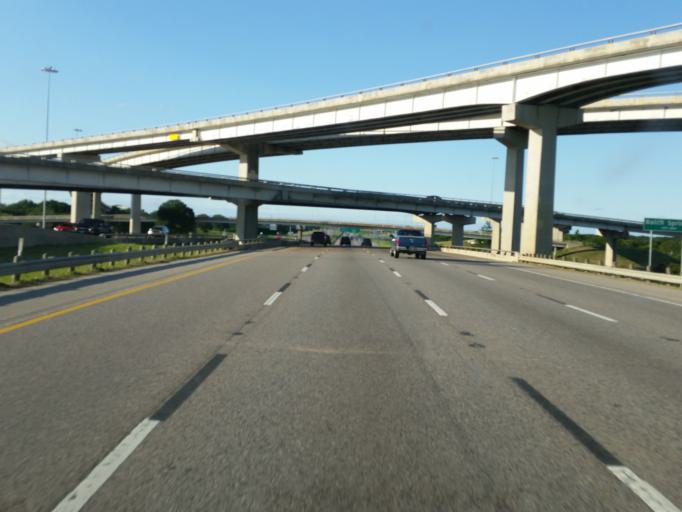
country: US
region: Texas
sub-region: Dallas County
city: Balch Springs
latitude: 32.6906
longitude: -96.6326
